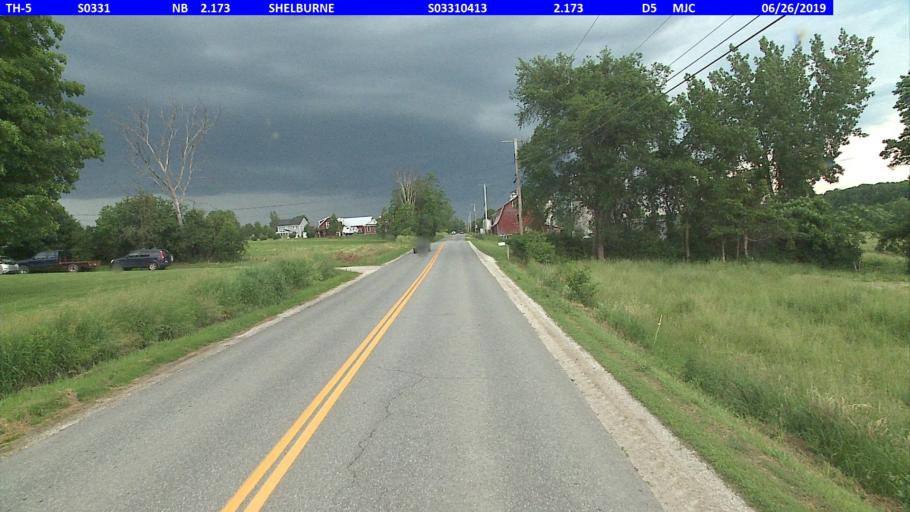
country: US
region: Vermont
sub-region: Chittenden County
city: South Burlington
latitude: 44.4017
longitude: -73.1786
